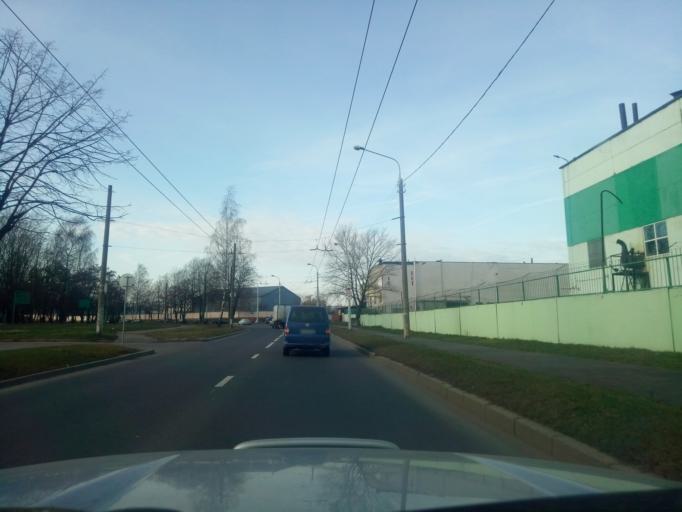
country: BY
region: Minsk
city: Novoye Medvezhino
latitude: 53.8846
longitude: 27.4921
